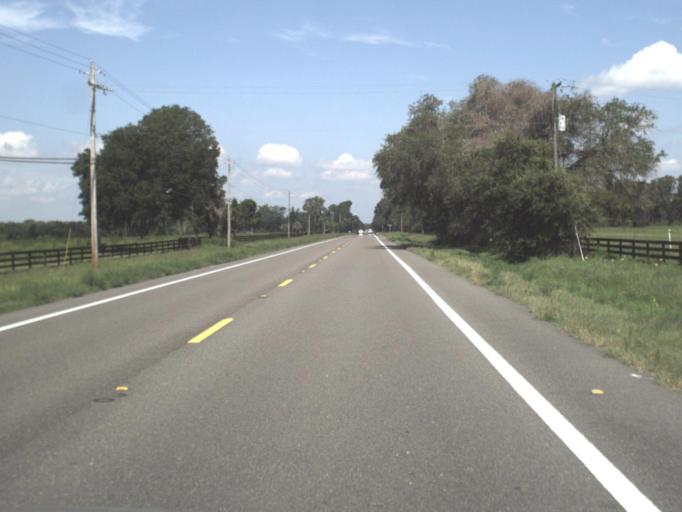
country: US
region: Florida
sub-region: Clay County
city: Green Cove Springs
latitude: 29.9803
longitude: -81.5543
